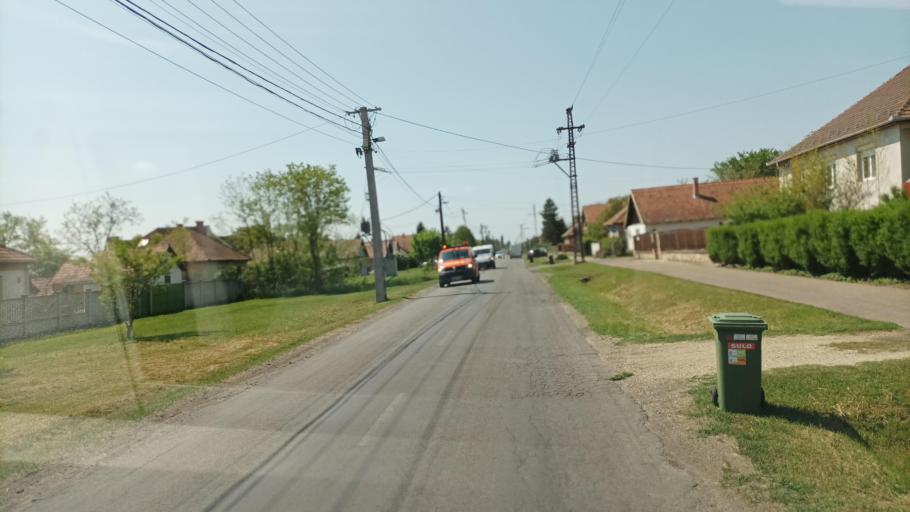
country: HU
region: Pest
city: Szentmartonkata
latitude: 47.4398
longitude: 19.6884
